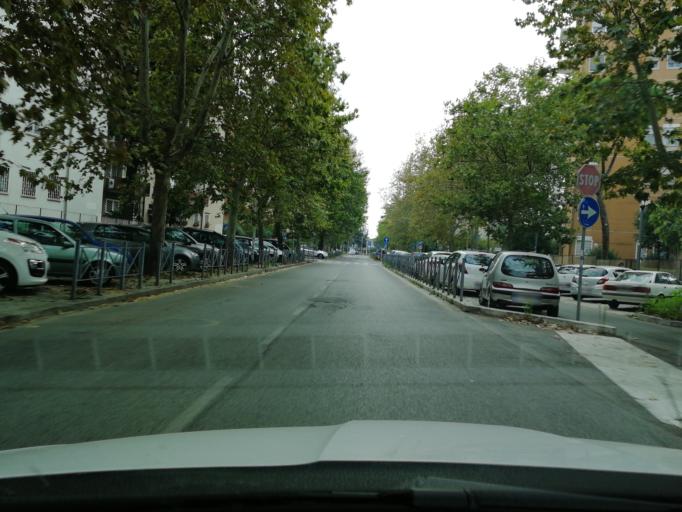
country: IT
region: Latium
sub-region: Citta metropolitana di Roma Capitale
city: Rome
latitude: 41.8579
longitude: 12.5538
